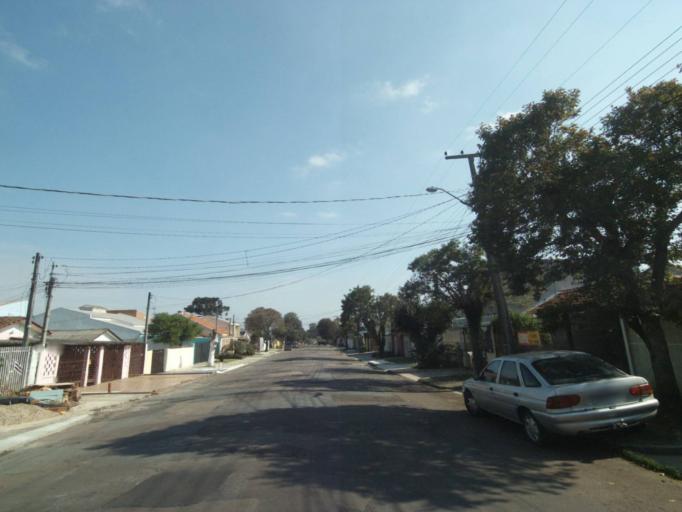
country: BR
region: Parana
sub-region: Curitiba
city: Curitiba
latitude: -25.4891
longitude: -49.3243
